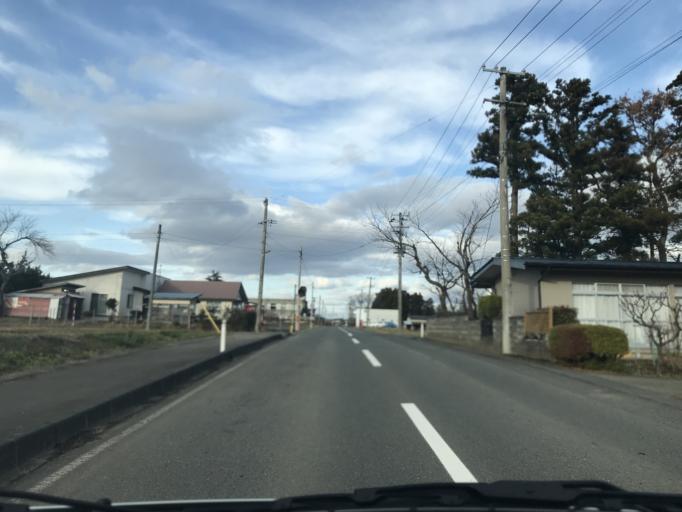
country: JP
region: Iwate
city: Mizusawa
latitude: 39.1850
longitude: 141.1058
